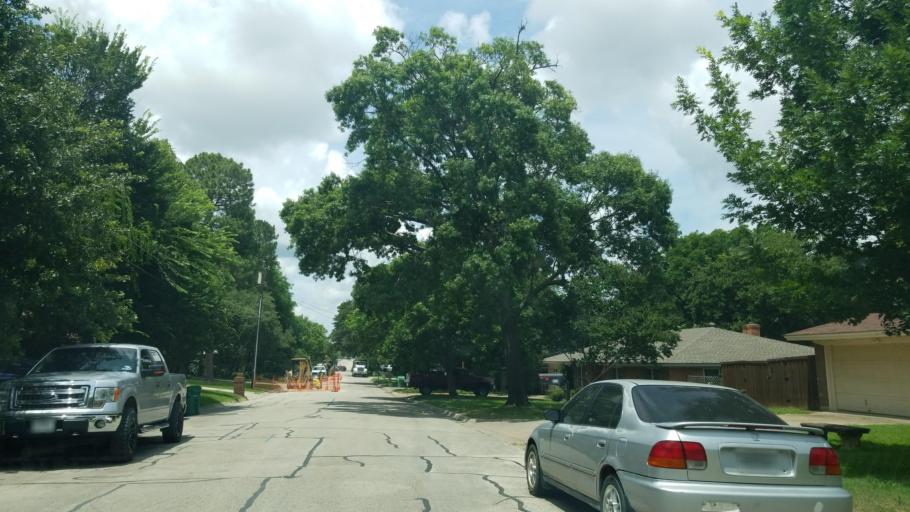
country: US
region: Texas
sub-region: Denton County
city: Denton
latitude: 33.2008
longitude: -97.1509
